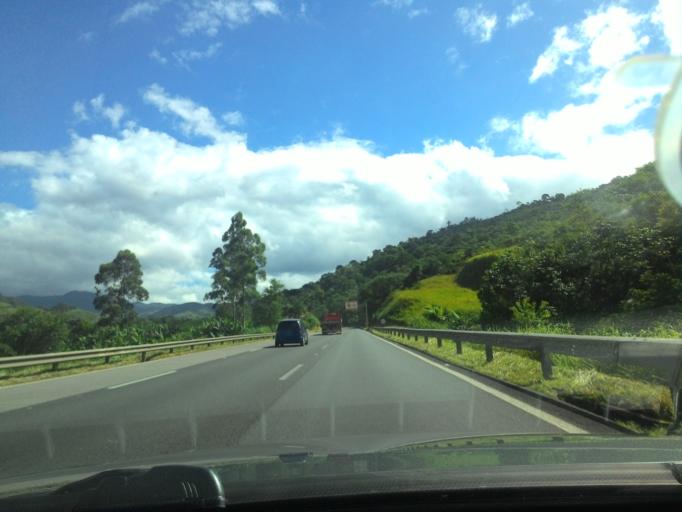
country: BR
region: Sao Paulo
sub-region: Cajati
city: Cajati
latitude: -24.8164
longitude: -48.2135
